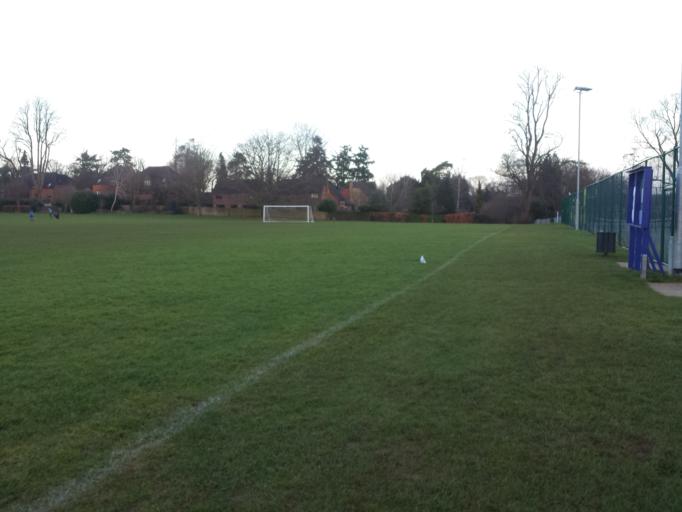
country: GB
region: England
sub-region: Surrey
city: Godalming
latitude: 51.1816
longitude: -0.6110
